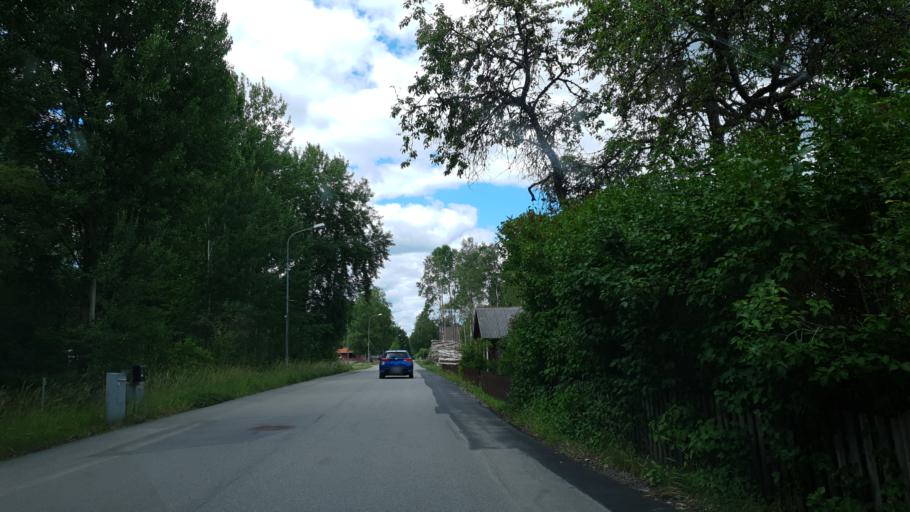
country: SE
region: Kalmar
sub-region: Emmaboda Kommun
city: Emmaboda
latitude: 56.9151
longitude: 15.5673
